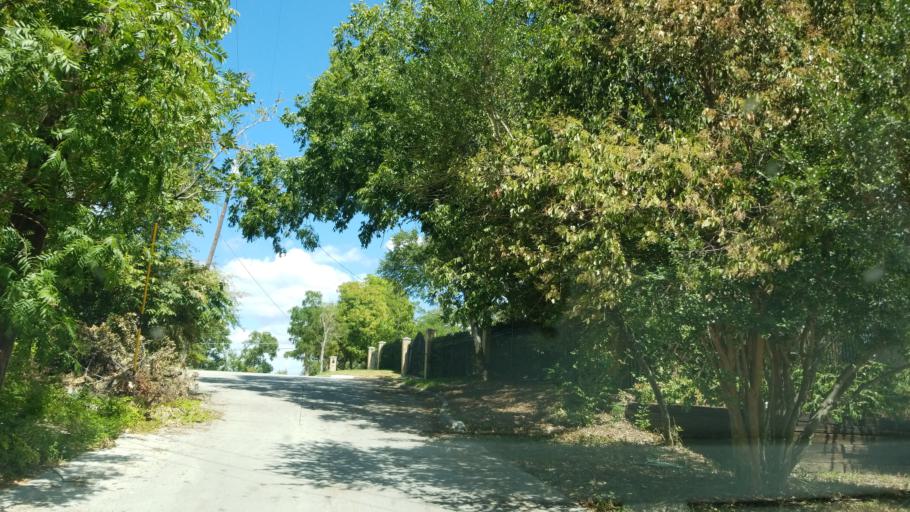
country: US
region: Texas
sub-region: Dallas County
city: Dallas
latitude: 32.7647
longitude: -96.8262
